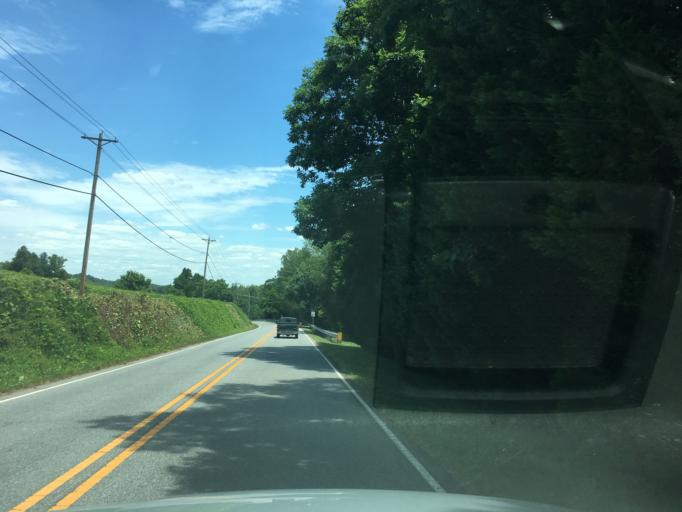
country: US
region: North Carolina
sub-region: Burke County
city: Glen Alpine
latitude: 35.6911
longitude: -81.7660
